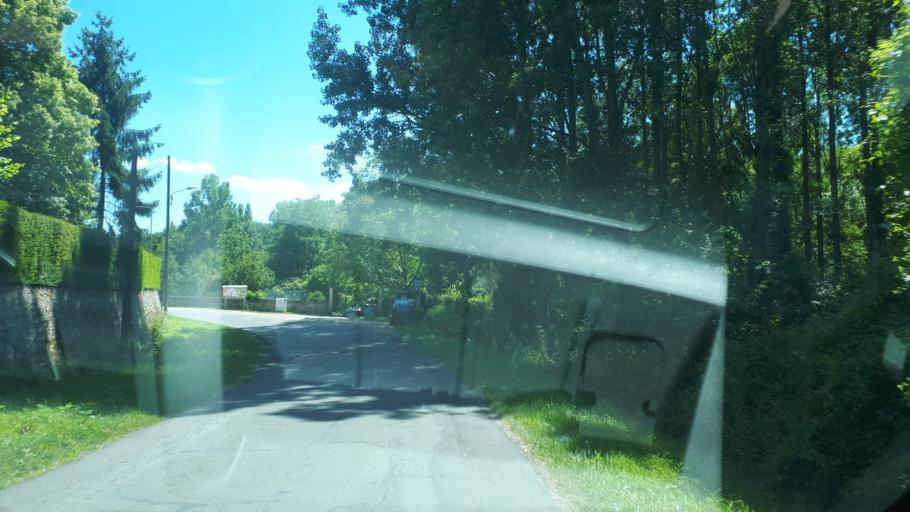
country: FR
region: Centre
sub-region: Departement du Loir-et-Cher
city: Saint-Sulpice-de-Pommeray
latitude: 47.5863
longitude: 1.2079
